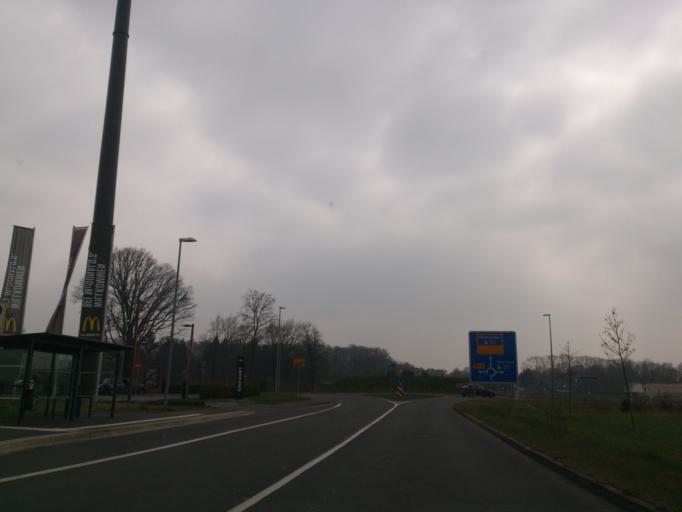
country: DE
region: North Rhine-Westphalia
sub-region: Regierungsbezirk Dusseldorf
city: Bruggen
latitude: 51.2127
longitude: 6.1342
